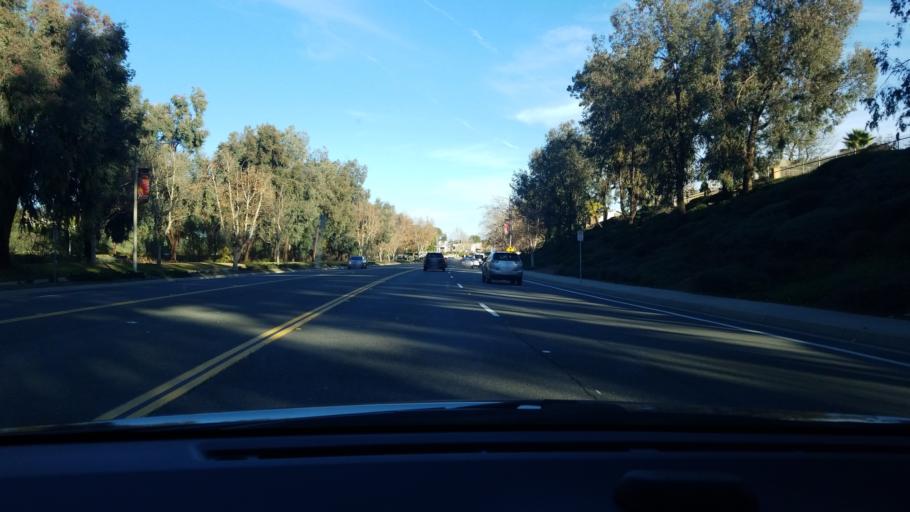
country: US
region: California
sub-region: Riverside County
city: Temecula
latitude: 33.5087
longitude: -117.1315
